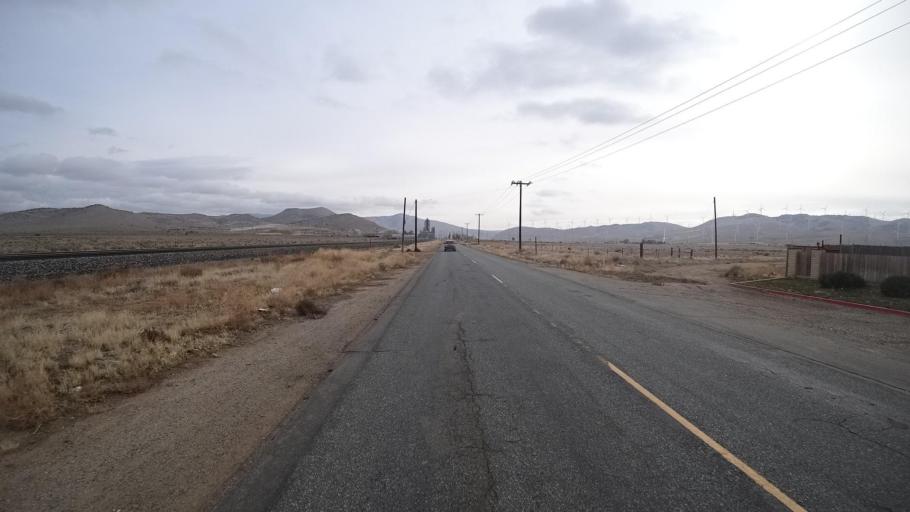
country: US
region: California
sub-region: Kern County
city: Tehachapi
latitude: 35.1240
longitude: -118.3880
